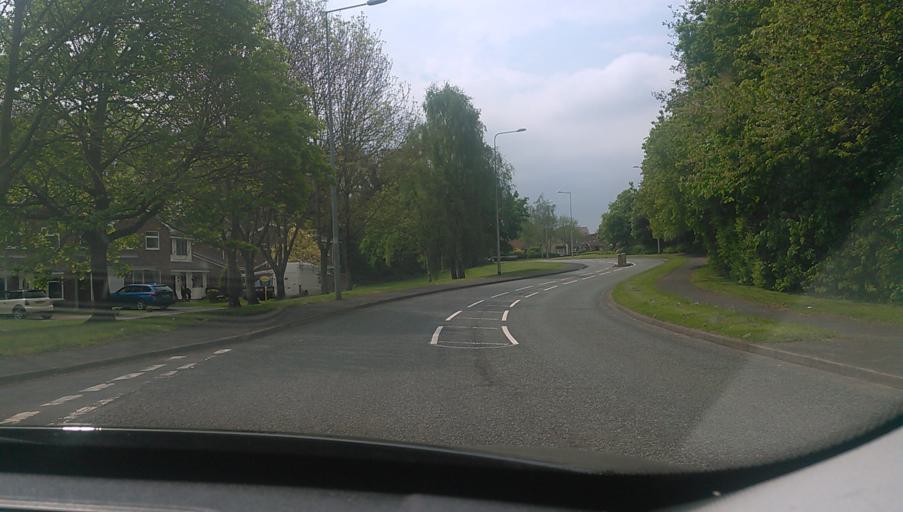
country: GB
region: England
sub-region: Shropshire
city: Hadley
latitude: 52.7145
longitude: -2.4970
